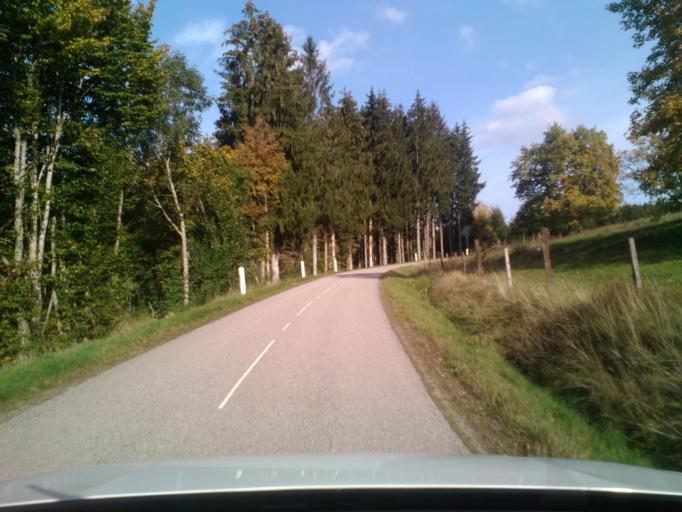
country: FR
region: Lorraine
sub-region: Departement des Vosges
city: Senones
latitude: 48.3773
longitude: 7.0521
